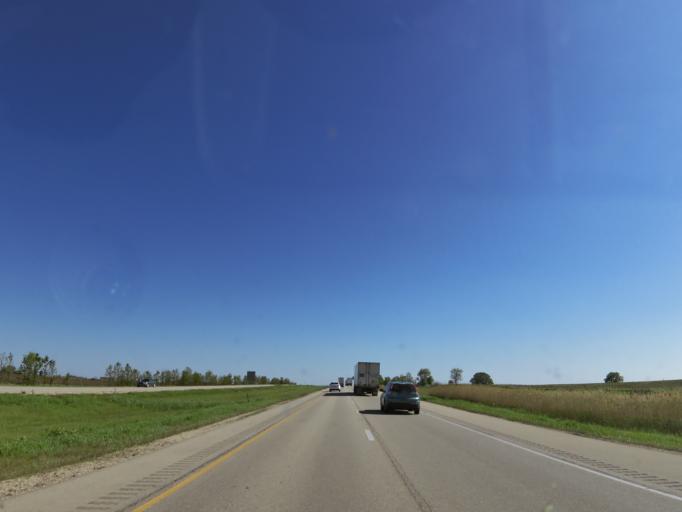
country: US
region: Illinois
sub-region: LaSalle County
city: Earlville
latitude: 41.7427
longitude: -89.0088
